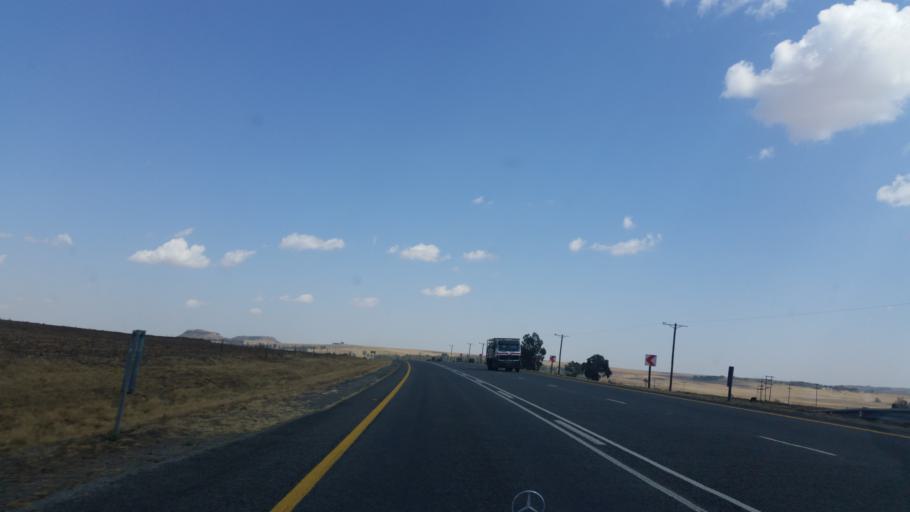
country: ZA
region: Orange Free State
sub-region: Thabo Mofutsanyana District Municipality
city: Bethlehem
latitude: -28.2711
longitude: 28.0899
